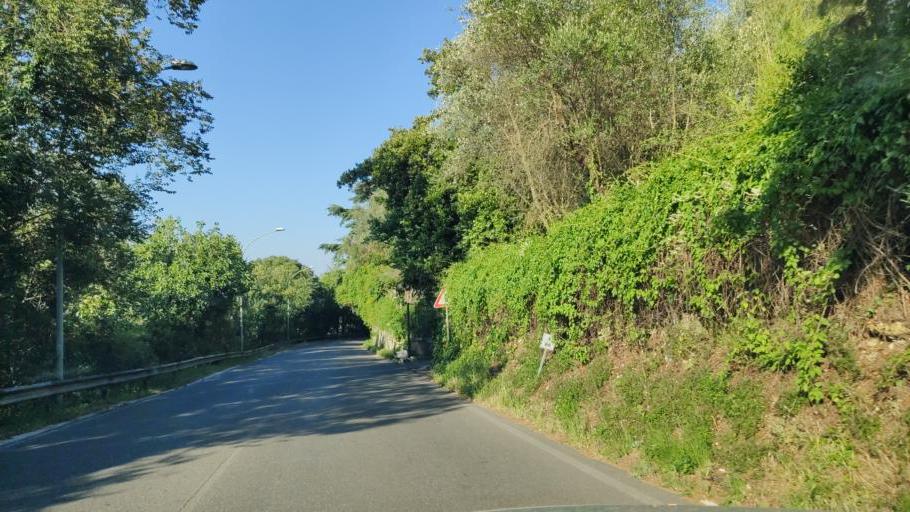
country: IT
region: Umbria
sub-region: Provincia di Terni
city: Narni
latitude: 42.5173
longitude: 12.5258
